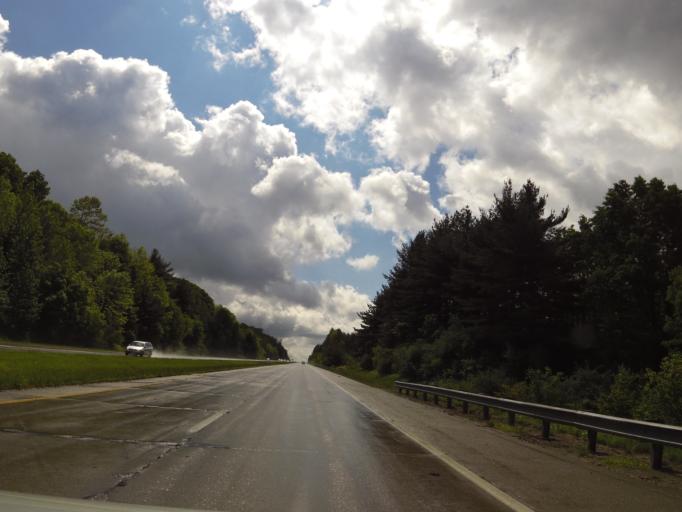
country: US
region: Ohio
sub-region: Athens County
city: Athens
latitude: 39.3585
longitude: -82.1020
